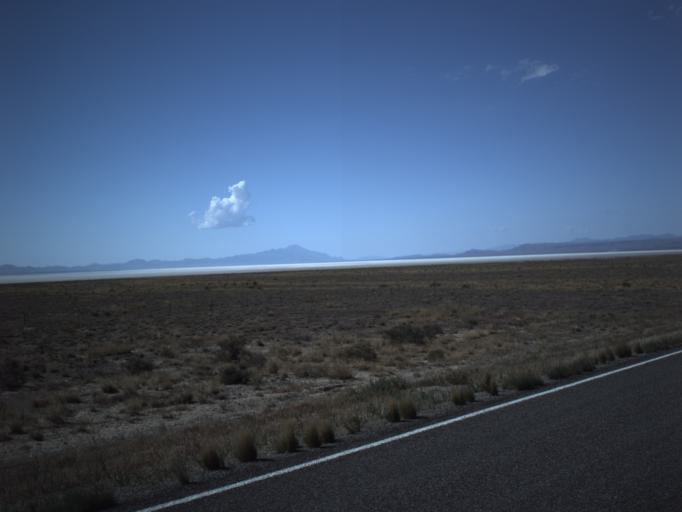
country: US
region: Utah
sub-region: Millard County
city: Delta
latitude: 39.1259
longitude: -113.1109
